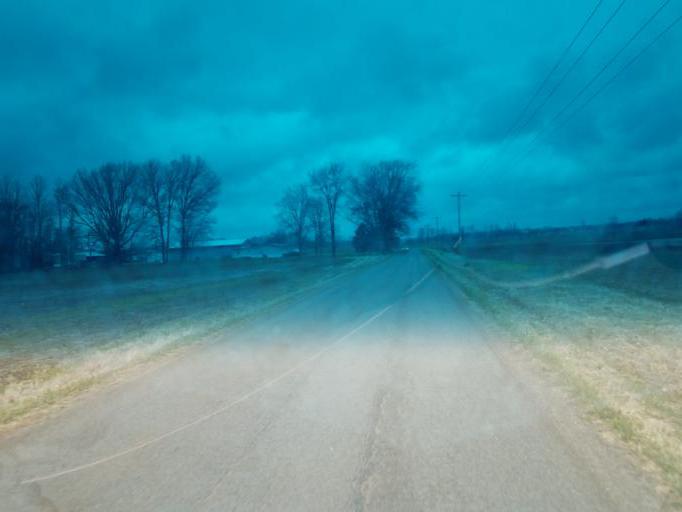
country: US
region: Ohio
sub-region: Morrow County
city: Mount Gilead
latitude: 40.4955
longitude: -82.7804
